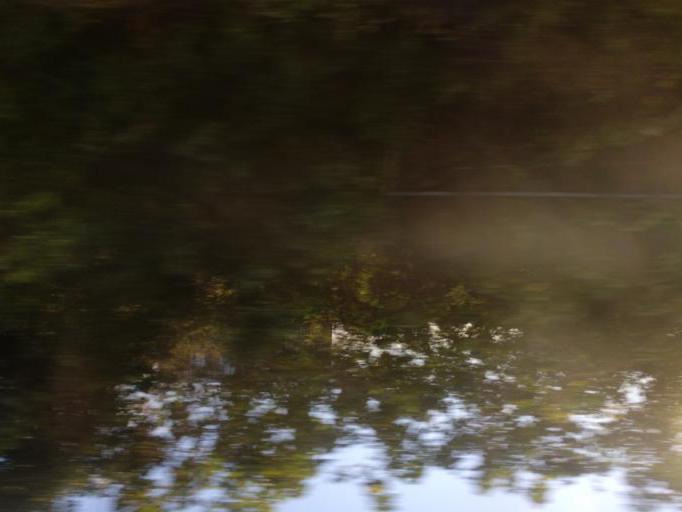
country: TW
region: Taiwan
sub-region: Hsinchu
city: Zhubei
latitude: 24.8436
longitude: 121.0124
